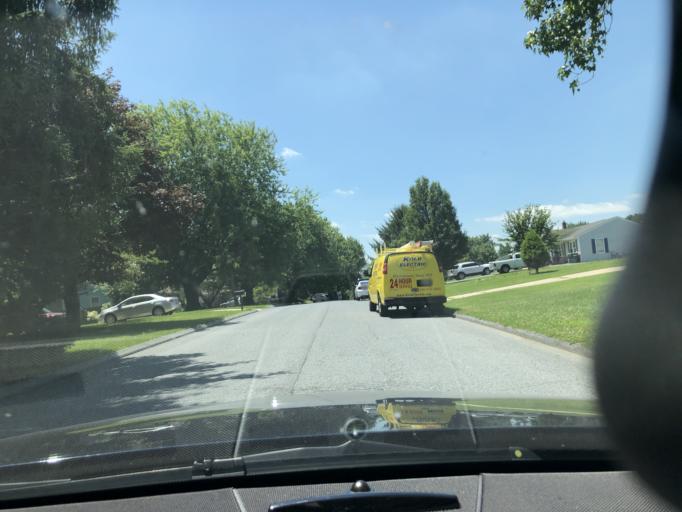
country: US
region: Maryland
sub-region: Carroll County
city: Westminster
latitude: 39.5526
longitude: -76.9705
